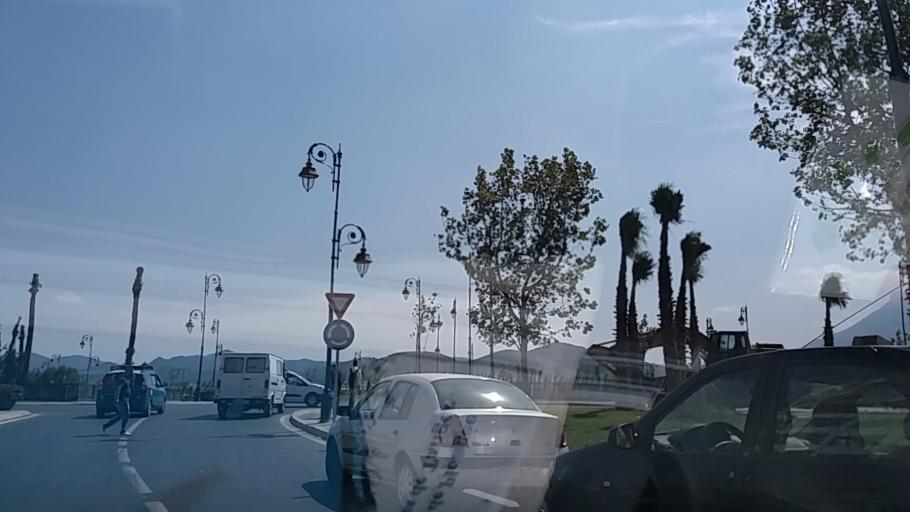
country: MA
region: Tanger-Tetouan
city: Tetouan
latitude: 35.5649
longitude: -5.3545
